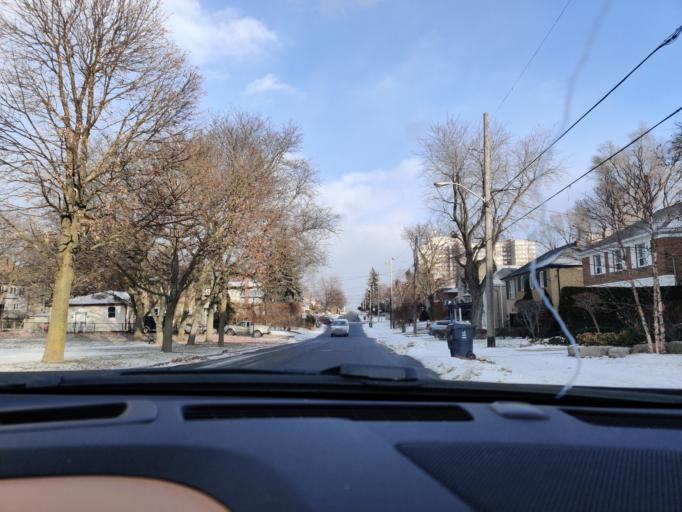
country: CA
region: Ontario
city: Toronto
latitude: 43.7167
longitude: -79.4339
